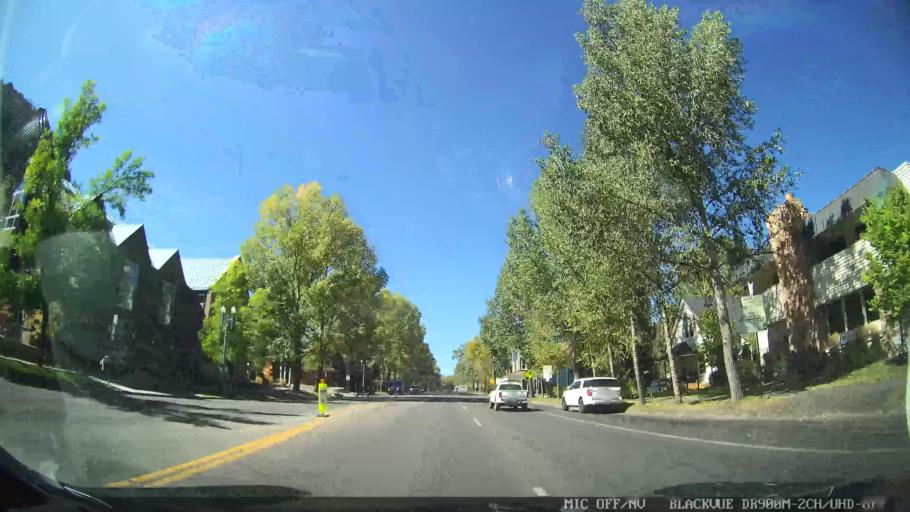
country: US
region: Colorado
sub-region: Pitkin County
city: Aspen
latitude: 39.1922
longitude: -106.8263
